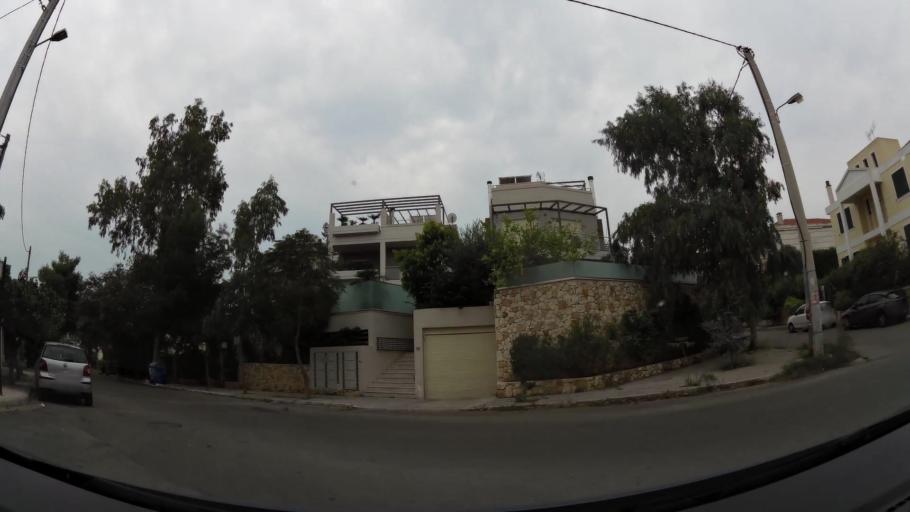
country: GR
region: Attica
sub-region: Nomarchia Athinas
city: Alimos
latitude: 37.9116
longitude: 23.7319
